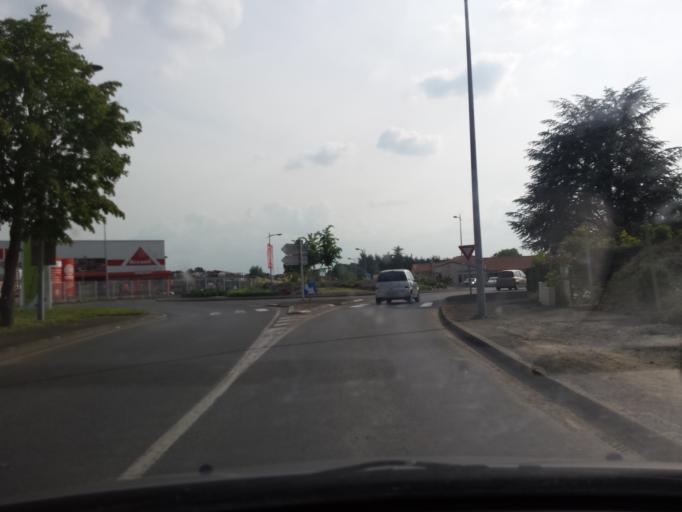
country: FR
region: Pays de la Loire
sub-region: Departement de Maine-et-Loire
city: Chemille-Melay
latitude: 47.2018
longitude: -0.7308
